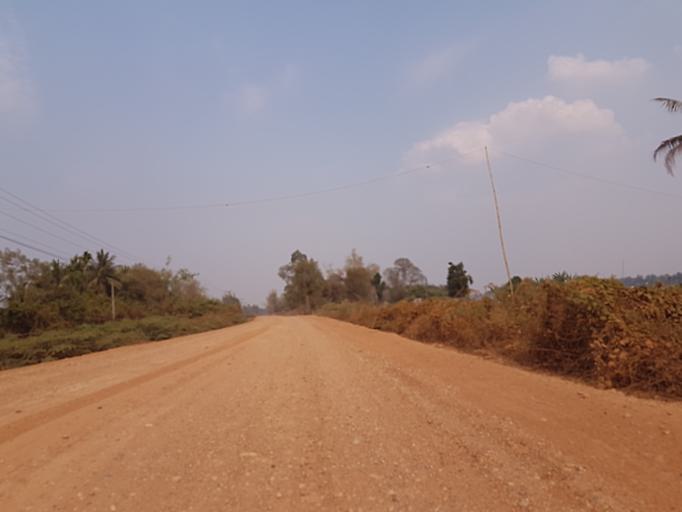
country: TH
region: Nong Khai
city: Nong Khai
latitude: 17.9748
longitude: 102.8534
